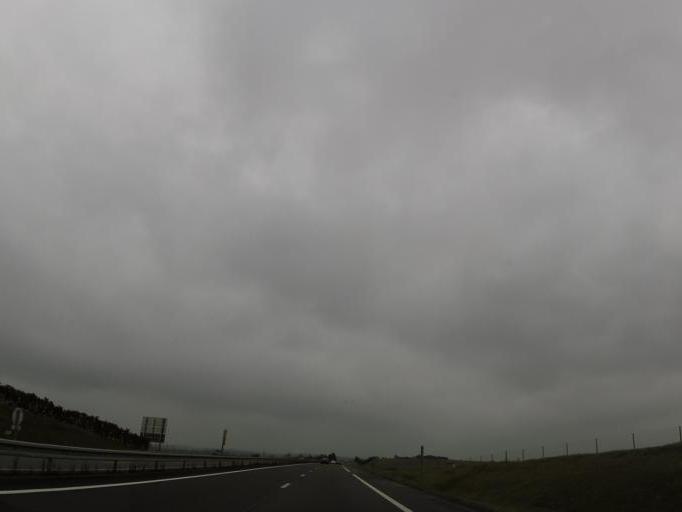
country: FR
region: Champagne-Ardenne
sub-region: Departement de la Marne
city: Sainte-Menehould
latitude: 49.0761
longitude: 4.8070
